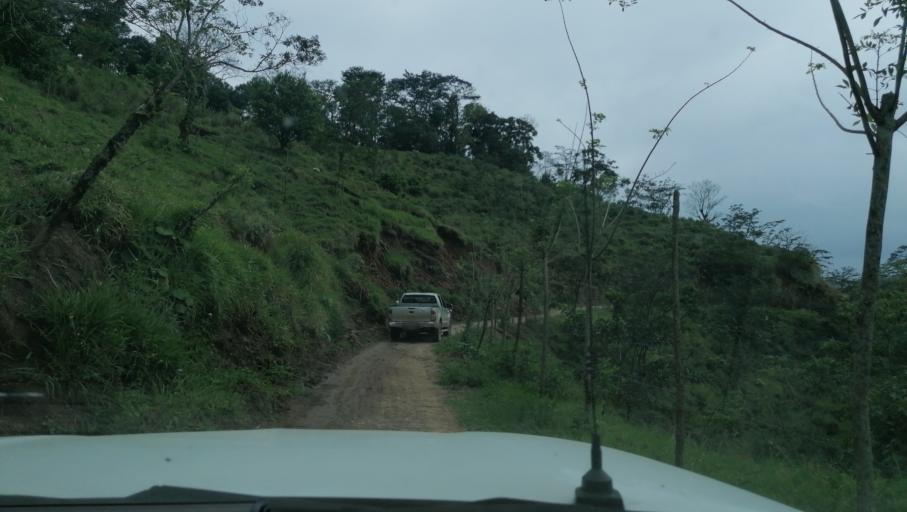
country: MX
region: Chiapas
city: Ostuacan
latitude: 17.3474
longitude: -93.3084
